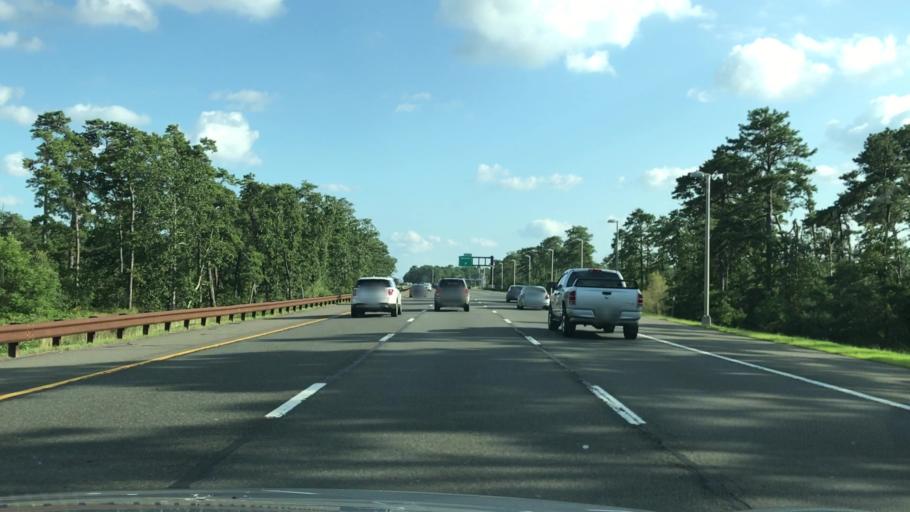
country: US
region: New Jersey
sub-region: Ocean County
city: South Toms River
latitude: 39.9115
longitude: -74.2123
